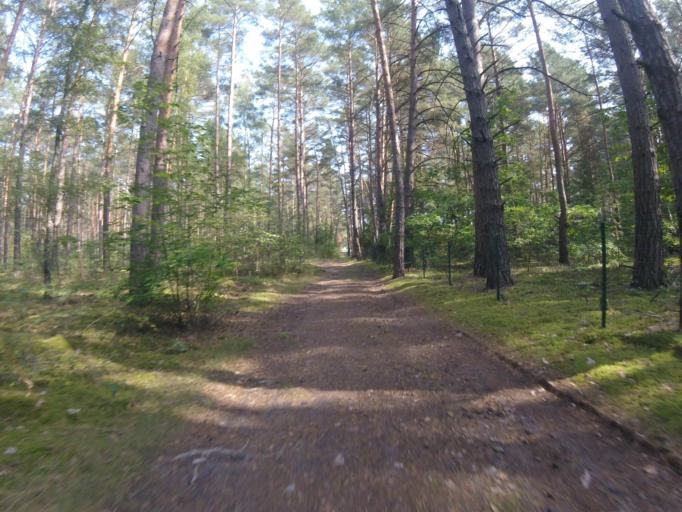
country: DE
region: Brandenburg
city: Bestensee
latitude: 52.2572
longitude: 13.6973
